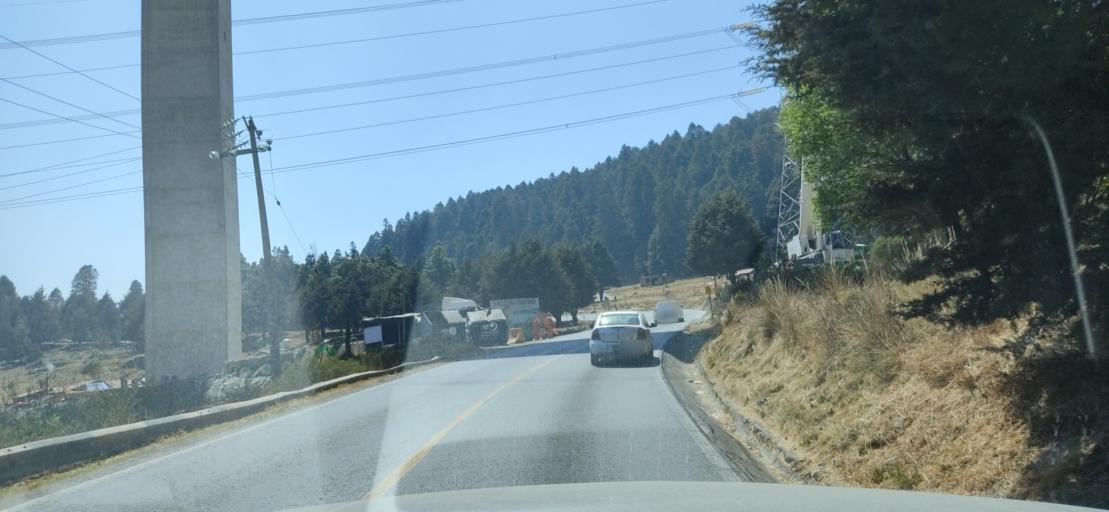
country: MX
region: Mexico
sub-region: Ocoyoacac
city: San Jeronimo Acazulco
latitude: 19.2951
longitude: -99.3751
